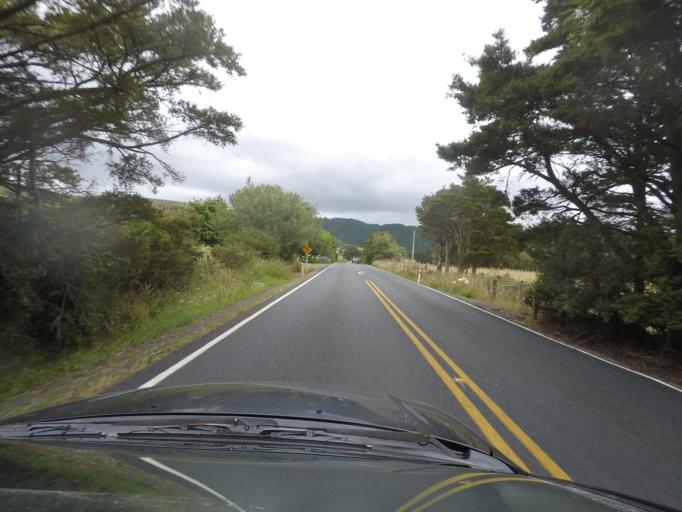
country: NZ
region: Auckland
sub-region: Auckland
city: Wellsford
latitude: -36.2880
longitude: 174.6295
